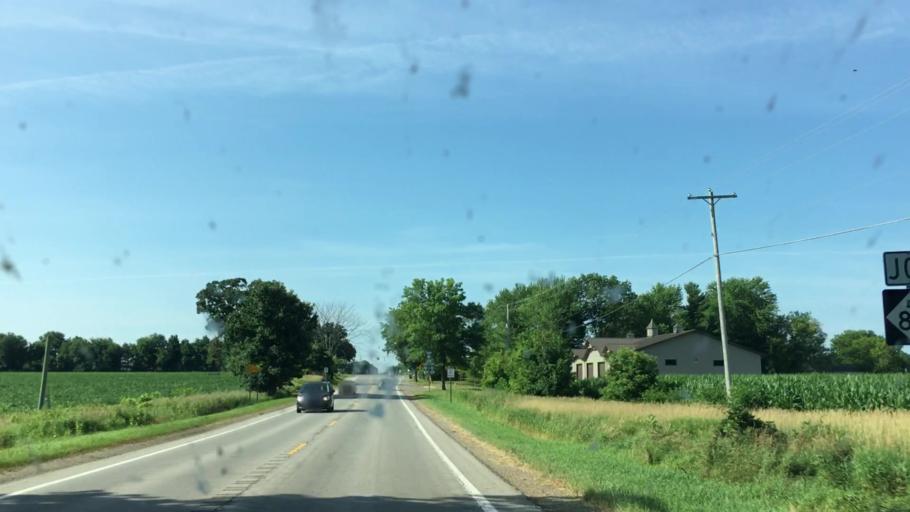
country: US
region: Michigan
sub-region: Kalamazoo County
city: South Gull Lake
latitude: 42.3936
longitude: -85.4552
